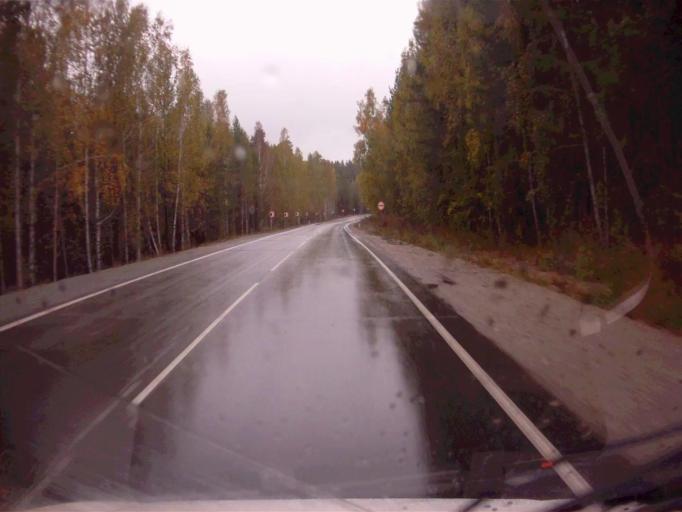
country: RU
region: Chelyabinsk
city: Kyshtym
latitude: 55.6546
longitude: 60.5753
